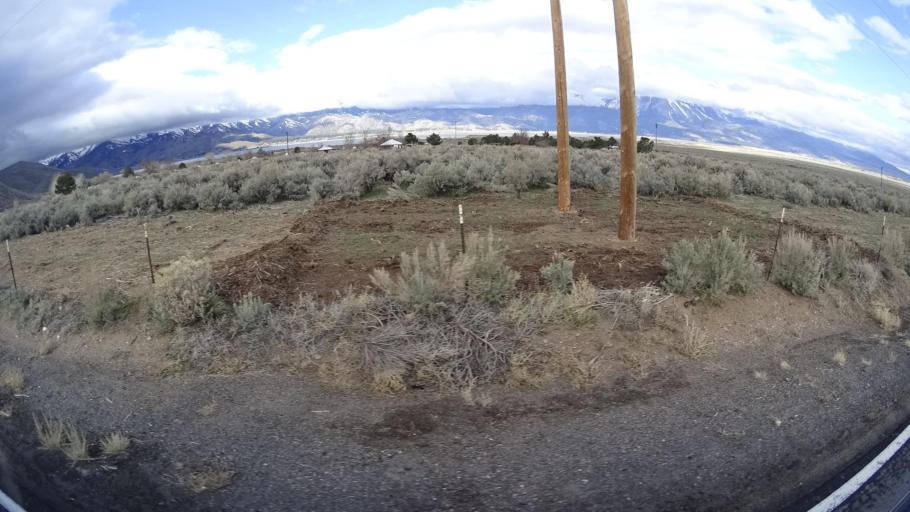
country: US
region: Nevada
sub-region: Carson City
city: Carson City
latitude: 39.2473
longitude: -119.7568
